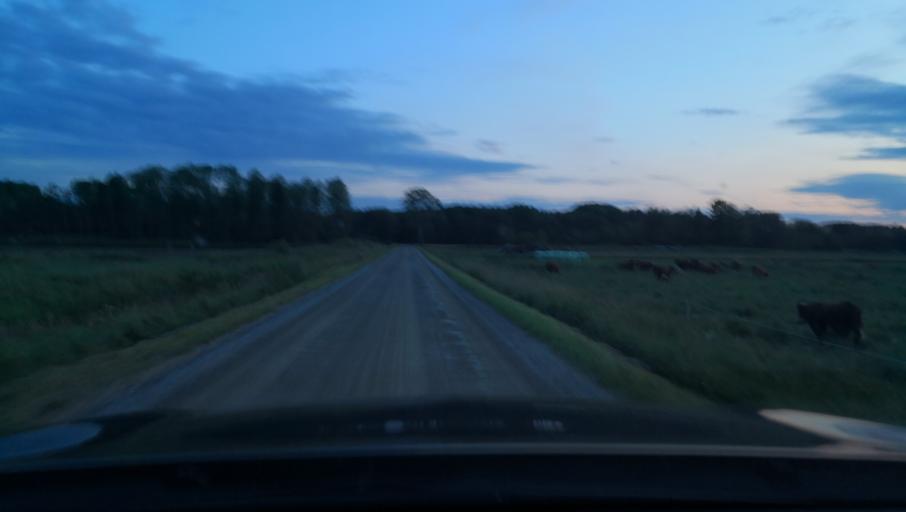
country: SE
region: Uppsala
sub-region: Osthammars Kommun
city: Bjorklinge
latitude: 60.0064
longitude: 17.3887
